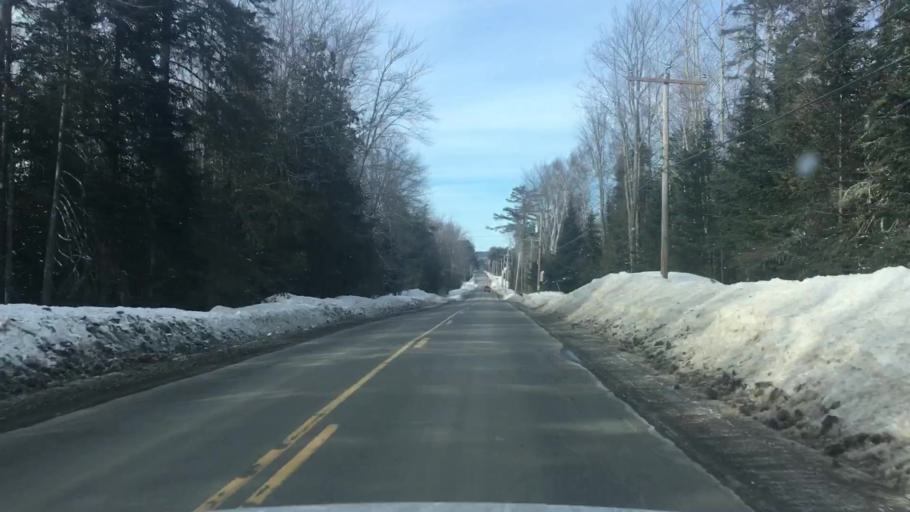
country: US
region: Maine
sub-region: Penobscot County
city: Charleston
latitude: 45.0478
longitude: -69.0293
